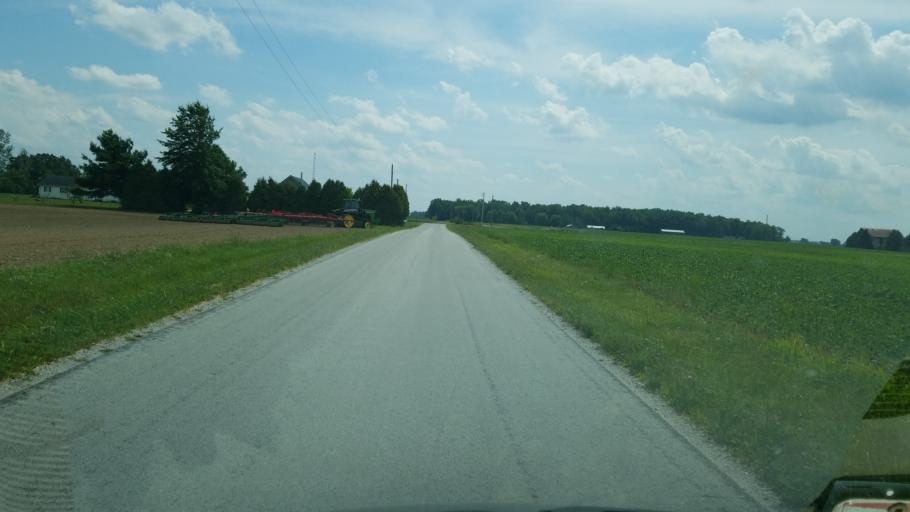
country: US
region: Ohio
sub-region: Wyandot County
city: Carey
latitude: 40.9069
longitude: -83.4671
